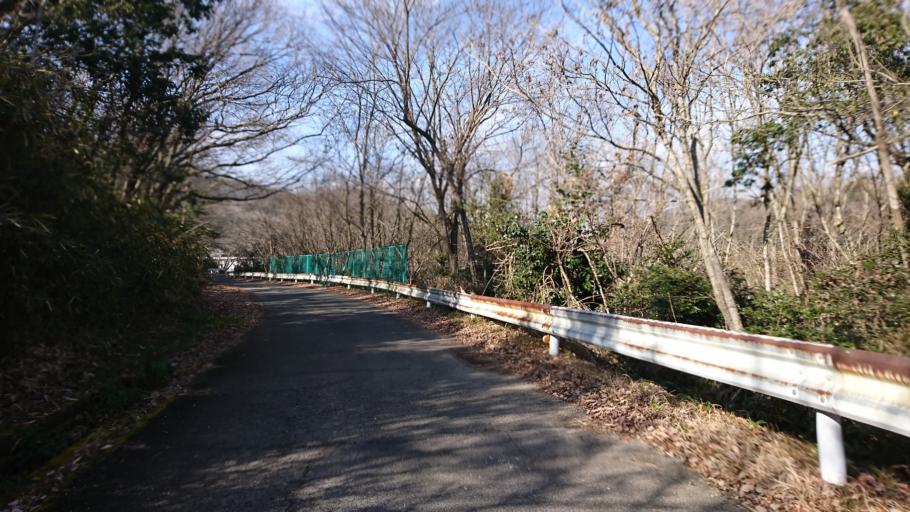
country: JP
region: Hyogo
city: Ono
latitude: 34.8337
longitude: 134.8668
